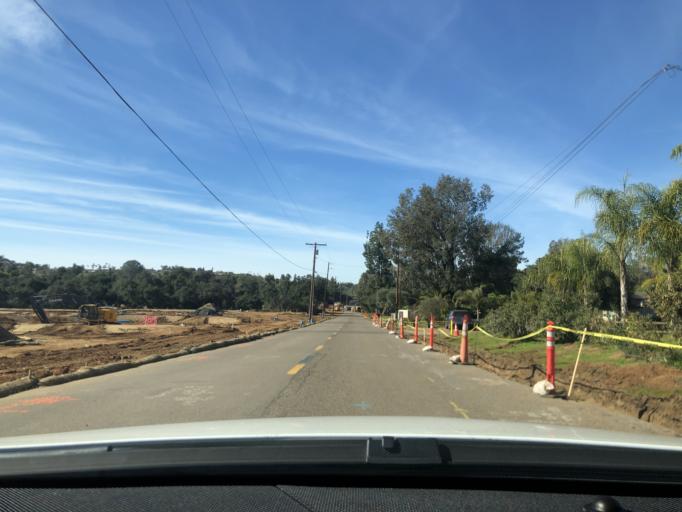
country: US
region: California
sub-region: San Diego County
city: Escondido
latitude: 33.0885
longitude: -117.0812
